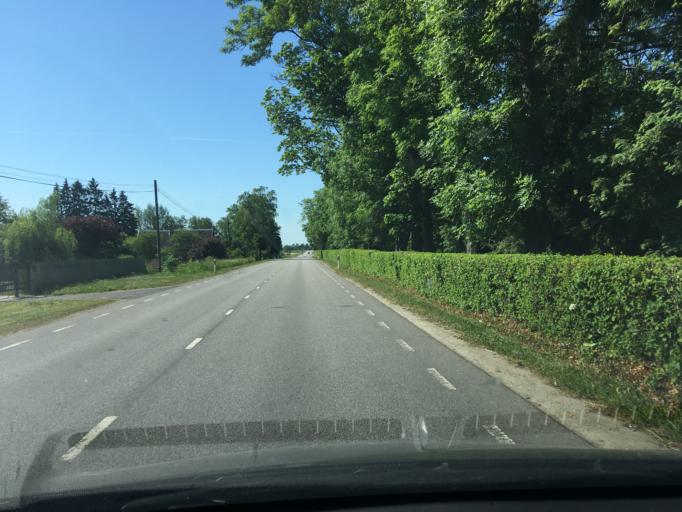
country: EE
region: Harju
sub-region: Raasiku vald
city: Raasiku
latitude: 59.3782
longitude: 25.1945
